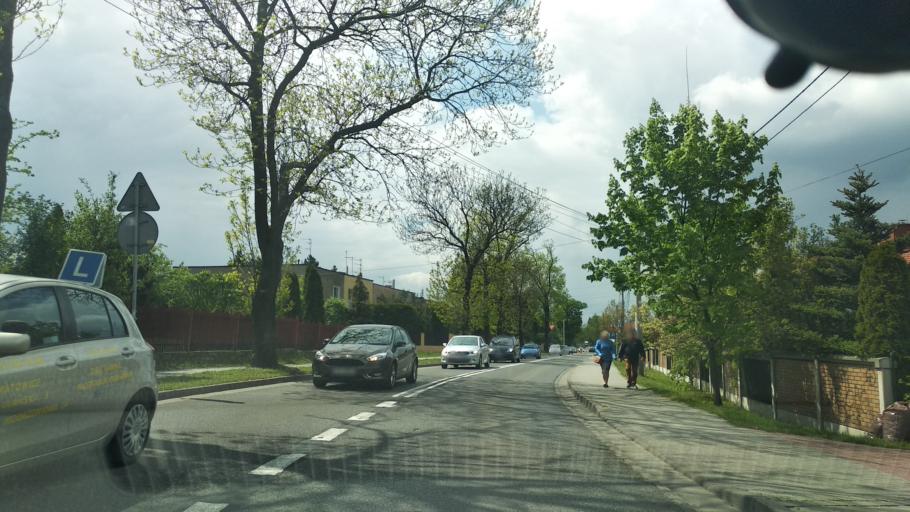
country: PL
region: Silesian Voivodeship
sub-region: Powiat mikolowski
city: Mikolow
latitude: 50.2298
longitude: 18.9472
